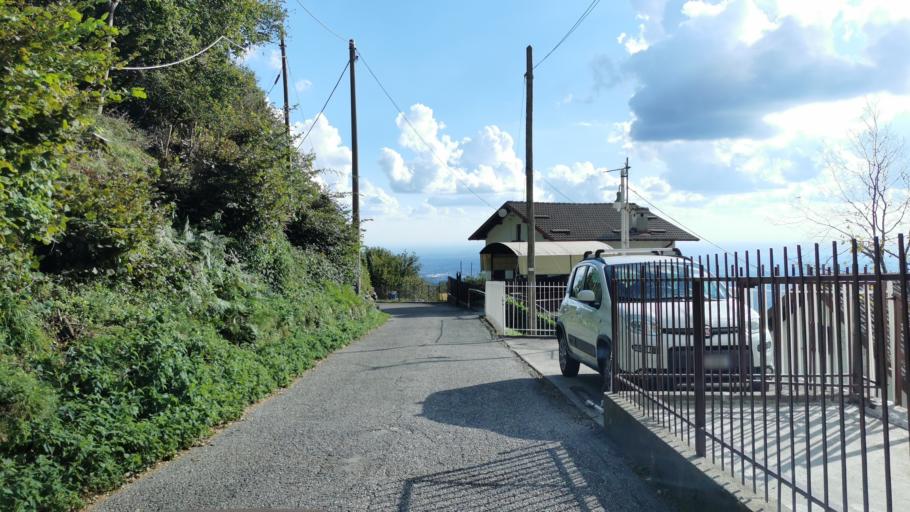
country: IT
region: Lombardy
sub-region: Provincia di Como
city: Moltrasio
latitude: 45.8695
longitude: 9.0768
